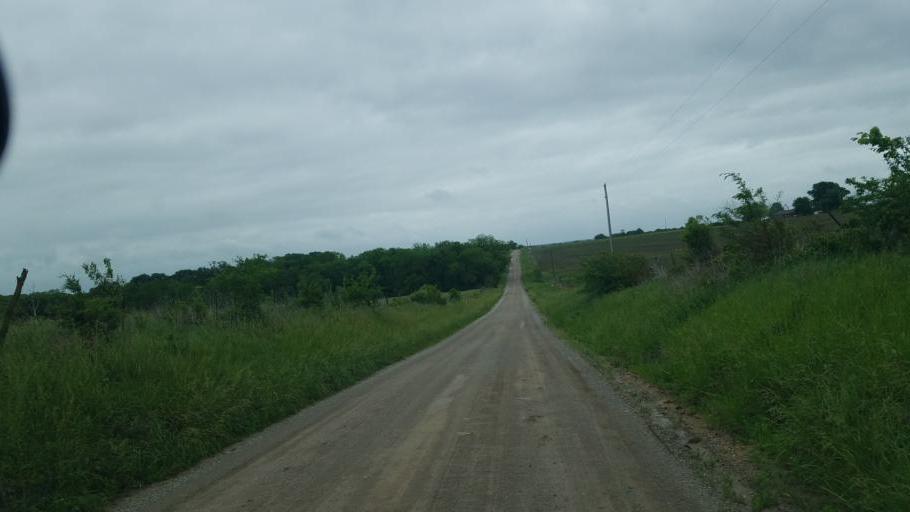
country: US
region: Missouri
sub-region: Carroll County
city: Carrollton
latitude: 39.4852
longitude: -93.5000
